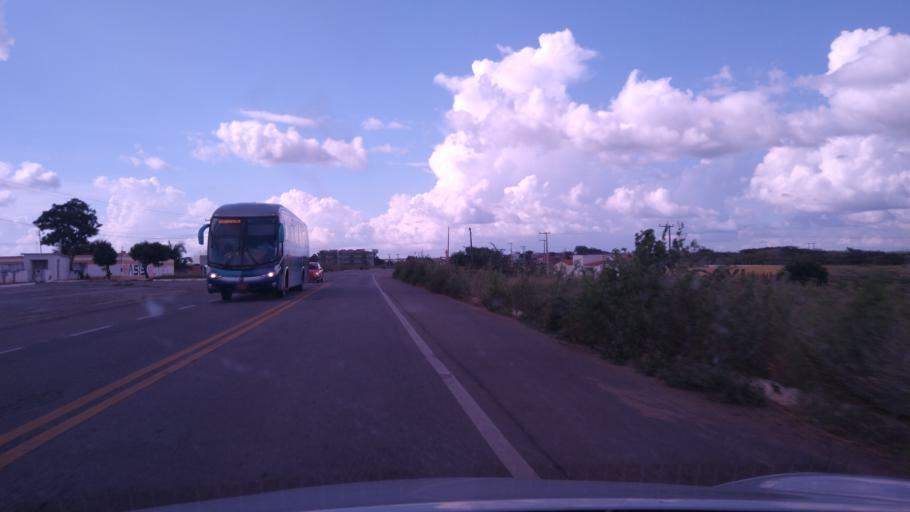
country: BR
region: Ceara
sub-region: Caninde
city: Caninde
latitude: -4.3869
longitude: -39.3126
